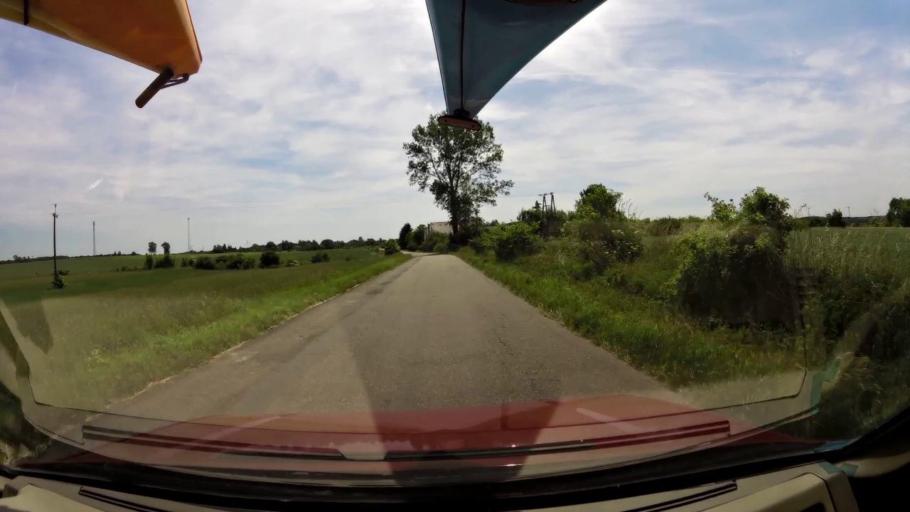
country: PL
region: West Pomeranian Voivodeship
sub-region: Powiat slawienski
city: Darlowo
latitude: 54.3227
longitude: 16.3978
